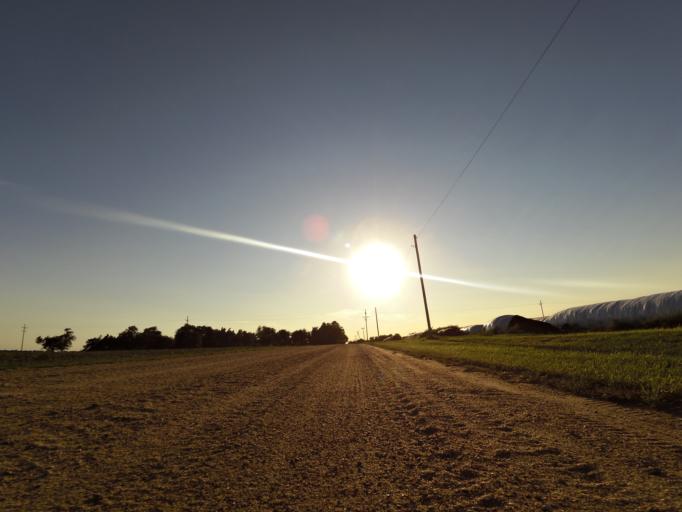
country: US
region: Kansas
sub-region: Reno County
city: South Hutchinson
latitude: 38.0136
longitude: -98.0303
